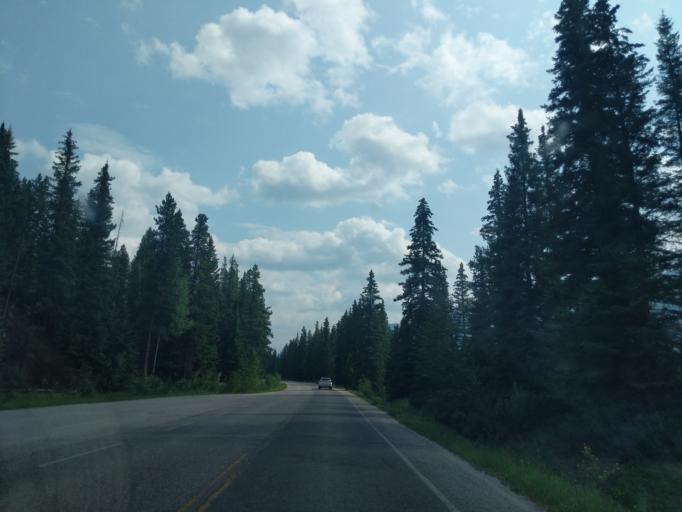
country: CA
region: Alberta
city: Banff
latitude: 51.2124
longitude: -115.7593
